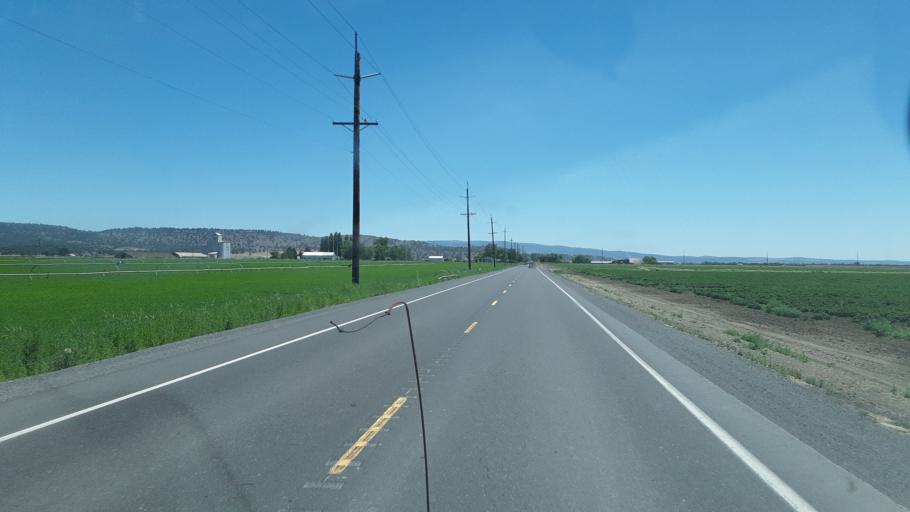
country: US
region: California
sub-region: Siskiyou County
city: Tulelake
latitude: 42.0240
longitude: -121.5704
